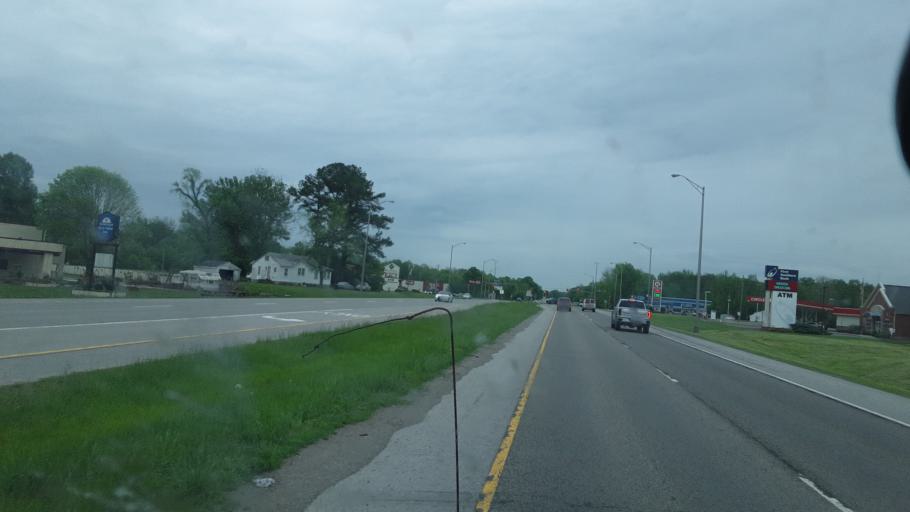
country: US
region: Illinois
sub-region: Jackson County
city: Murphysboro
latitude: 37.7652
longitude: -89.3203
